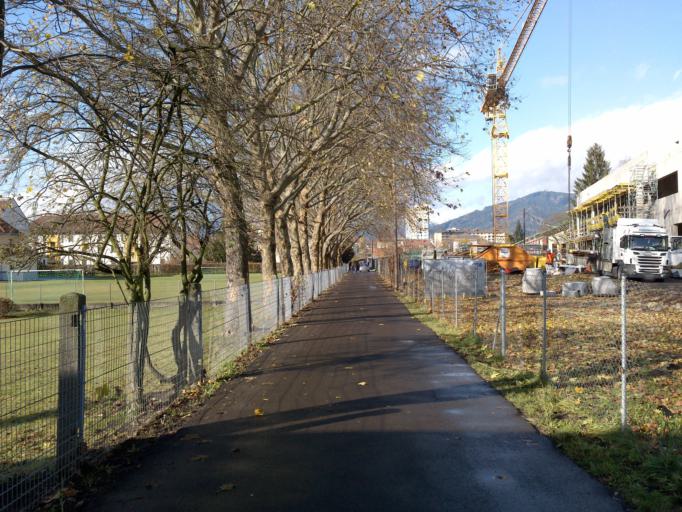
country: AT
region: Styria
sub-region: Politischer Bezirk Murtal
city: Apfelberg
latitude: 47.2089
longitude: 14.8356
